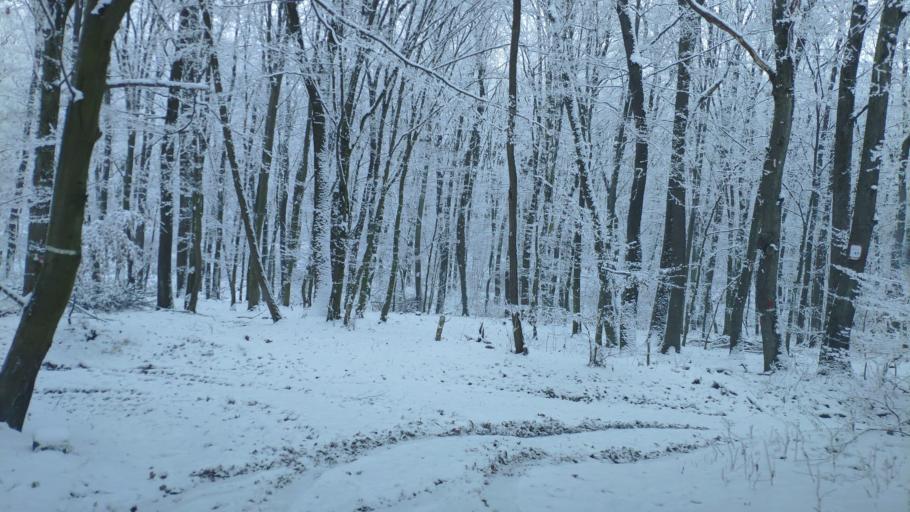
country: SK
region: Kosicky
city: Kosice
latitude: 48.6455
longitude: 21.1793
